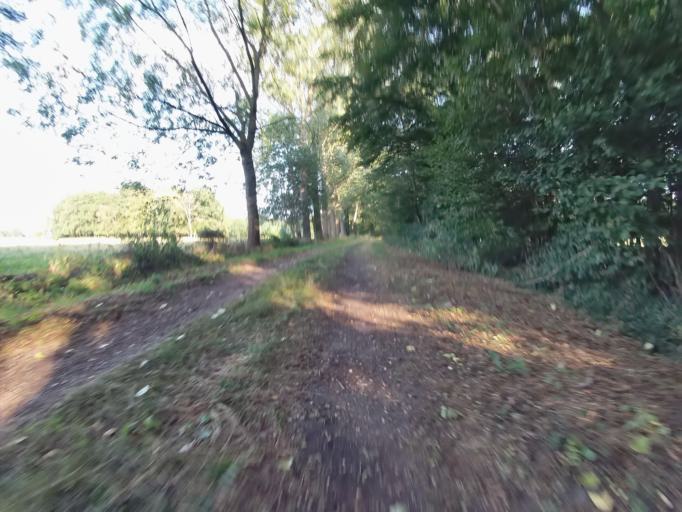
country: DE
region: North Rhine-Westphalia
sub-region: Regierungsbezirk Munster
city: Westerkappeln
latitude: 52.3191
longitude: 7.8378
